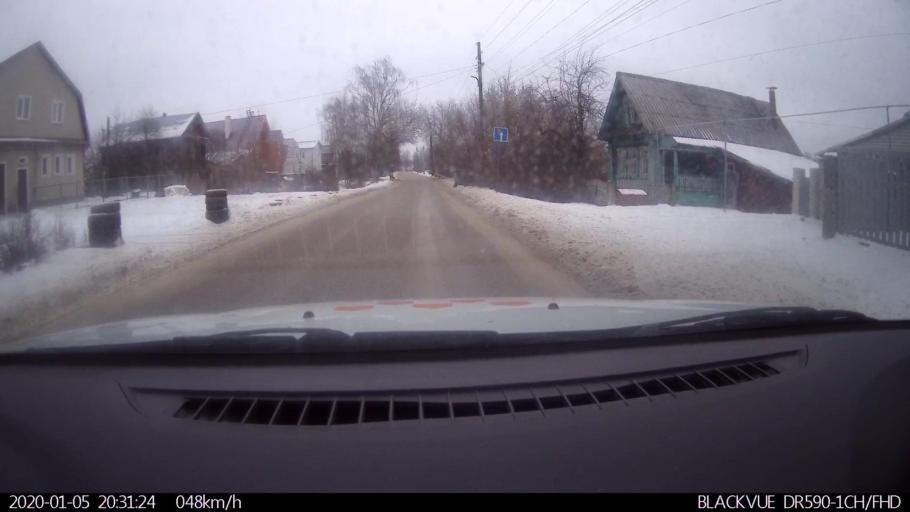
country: RU
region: Nizjnij Novgorod
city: Lukino
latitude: 56.4057
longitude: 43.7288
